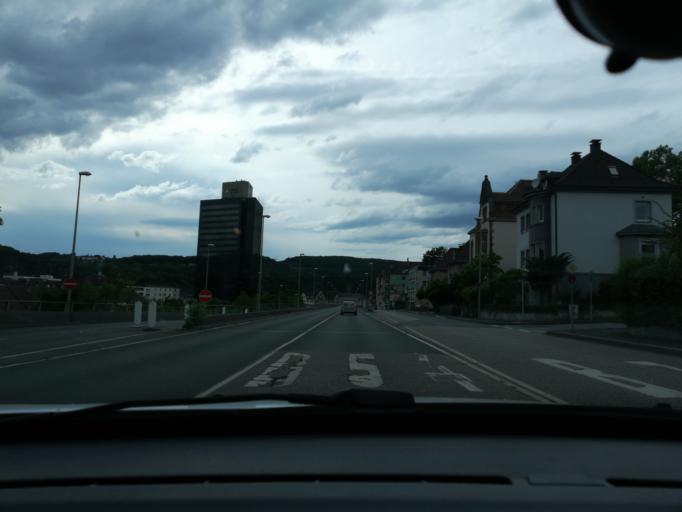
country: DE
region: North Rhine-Westphalia
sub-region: Regierungsbezirk Arnsberg
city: Hagen
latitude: 51.3633
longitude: 7.4688
